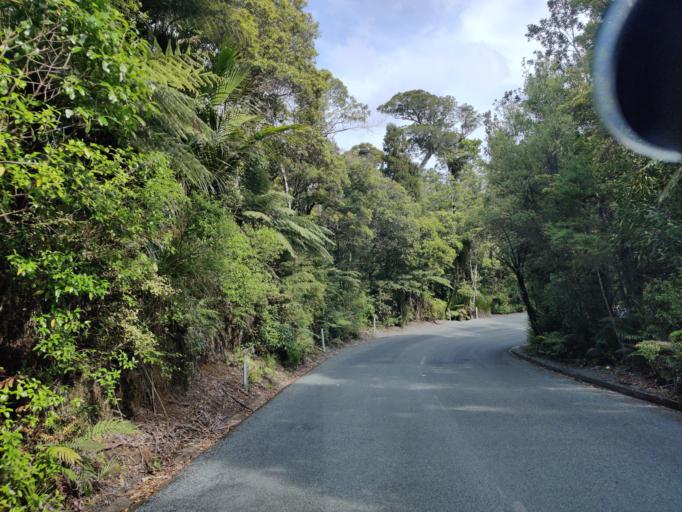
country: NZ
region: Northland
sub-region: Kaipara District
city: Dargaville
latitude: -35.6369
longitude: 173.5601
